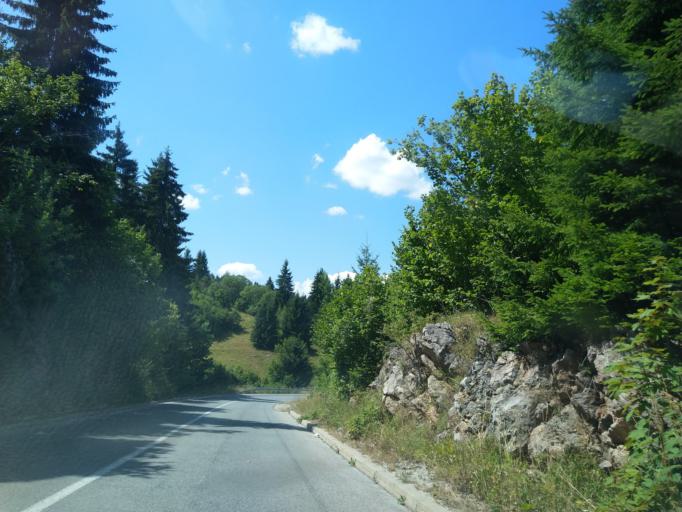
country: RS
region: Central Serbia
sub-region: Zlatiborski Okrug
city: Nova Varos
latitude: 43.4071
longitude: 19.8414
